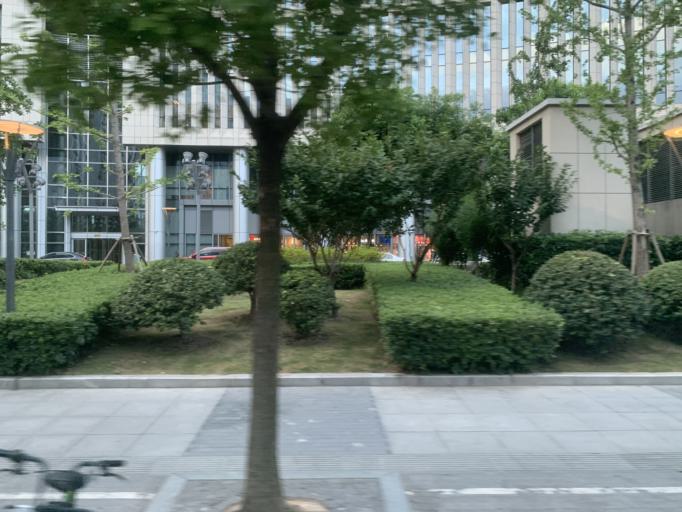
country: CN
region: Shanghai Shi
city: Pudong
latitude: 31.2317
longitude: 121.5245
